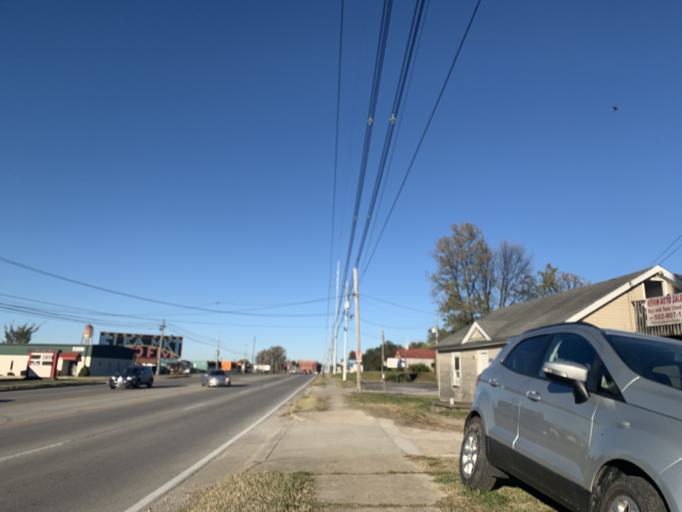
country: US
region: Kentucky
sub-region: Jefferson County
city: Shively
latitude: 38.2036
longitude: -85.7912
